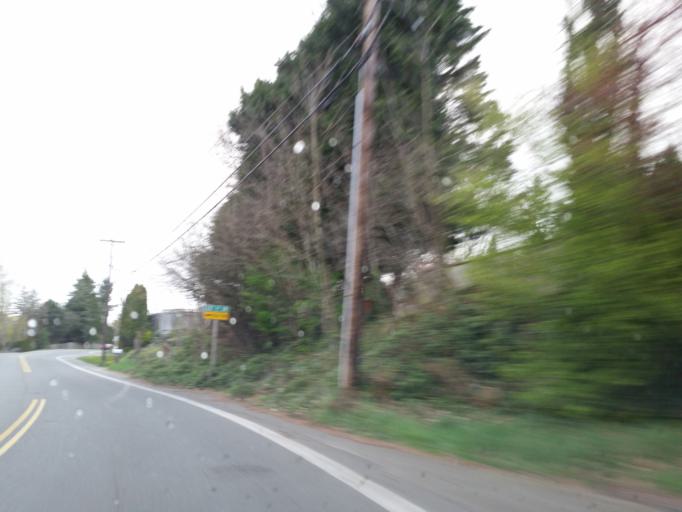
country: US
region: Washington
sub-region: Snohomish County
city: Alderwood Manor
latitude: 47.8103
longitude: -122.2790
